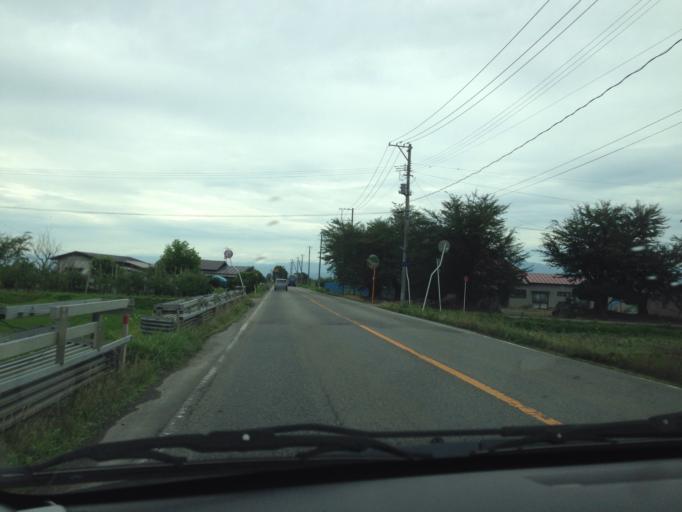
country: JP
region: Fukushima
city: Kitakata
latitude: 37.4589
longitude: 139.8793
